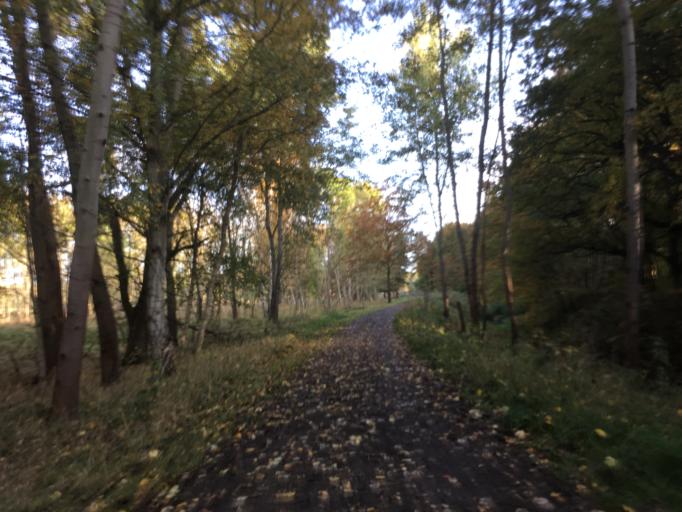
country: DE
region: Berlin
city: Buch
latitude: 52.6508
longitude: 13.4714
